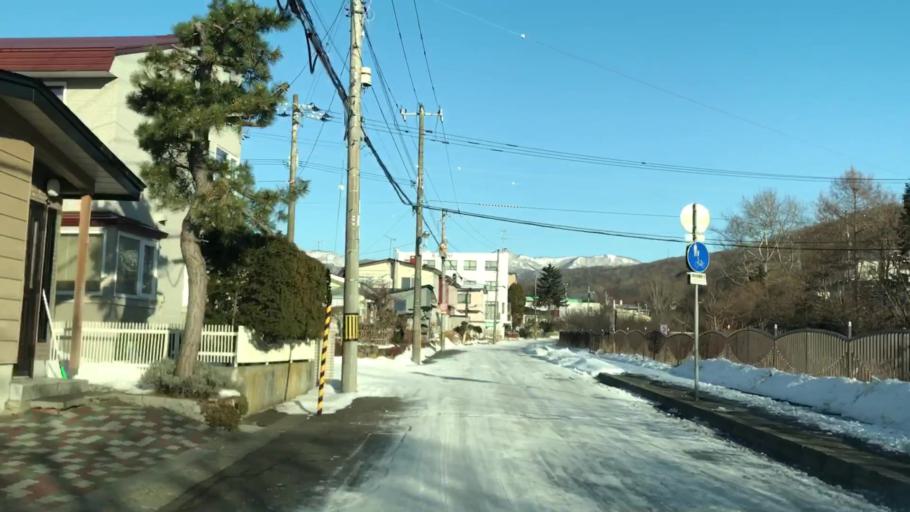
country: JP
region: Hokkaido
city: Muroran
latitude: 42.3743
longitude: 141.0376
